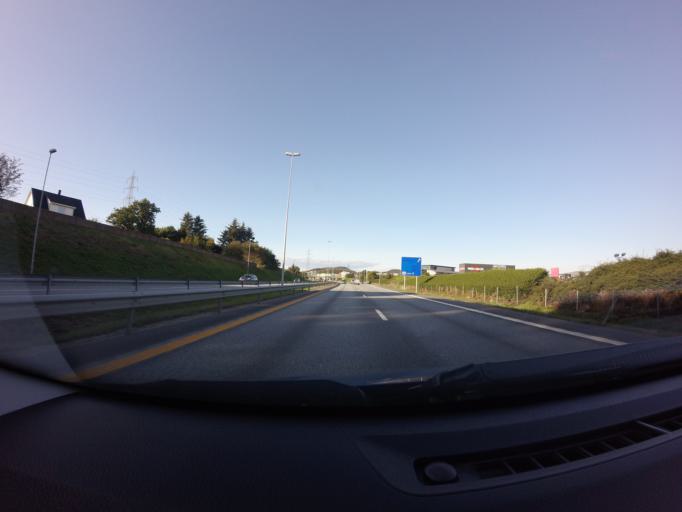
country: NO
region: Rogaland
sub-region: Sandnes
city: Sandnes
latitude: 58.8829
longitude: 5.7181
